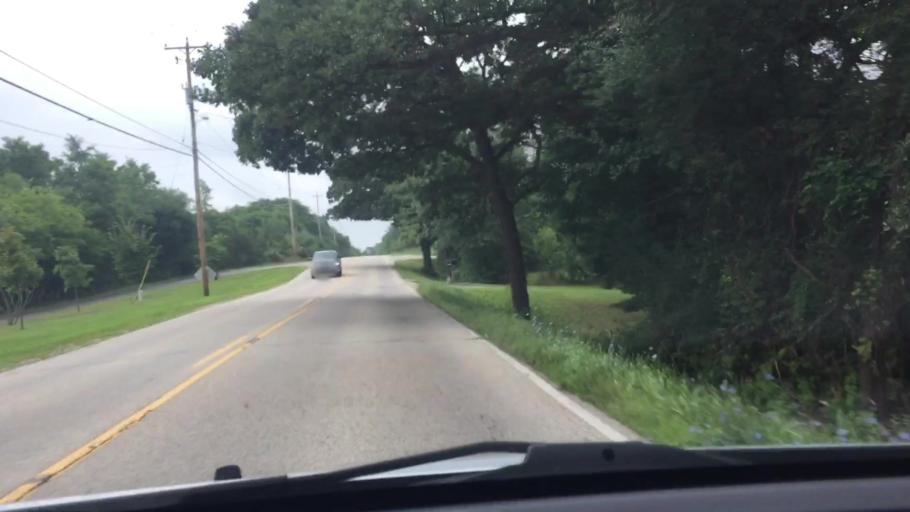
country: US
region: Wisconsin
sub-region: Waukesha County
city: Dousman
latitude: 43.0384
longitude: -88.4425
